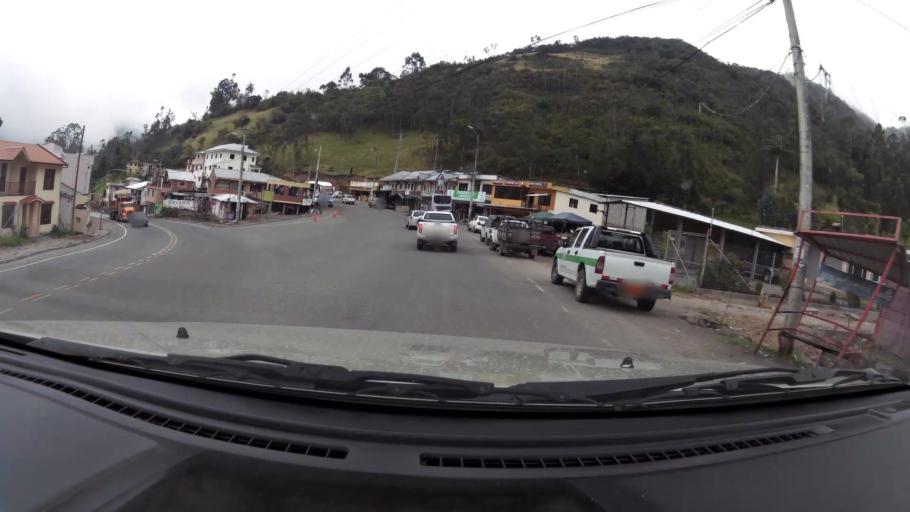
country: EC
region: Canar
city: Canar
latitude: -2.4601
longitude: -79.0042
